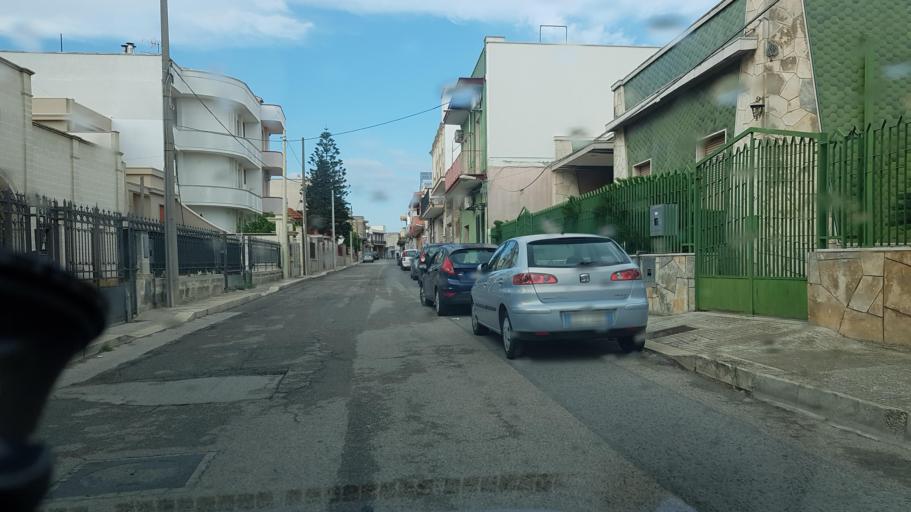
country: IT
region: Apulia
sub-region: Provincia di Brindisi
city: Torre Santa Susanna
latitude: 40.4642
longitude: 17.7358
